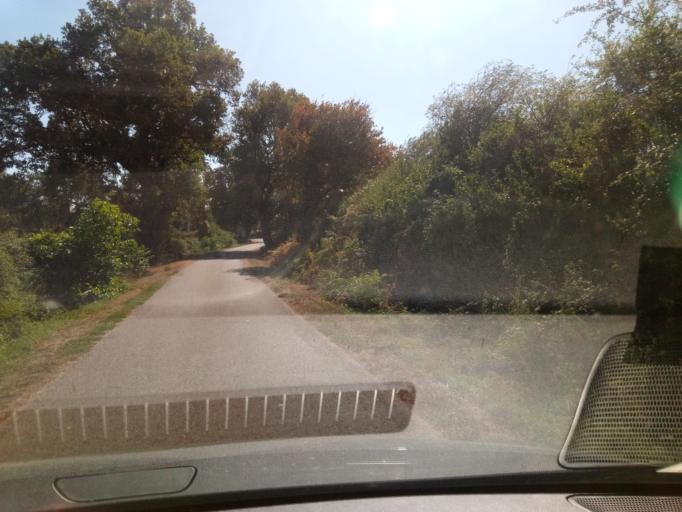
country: FR
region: Poitou-Charentes
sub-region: Departement de la Vienne
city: Lussac-les-Chateaux
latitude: 46.3954
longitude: 0.7542
